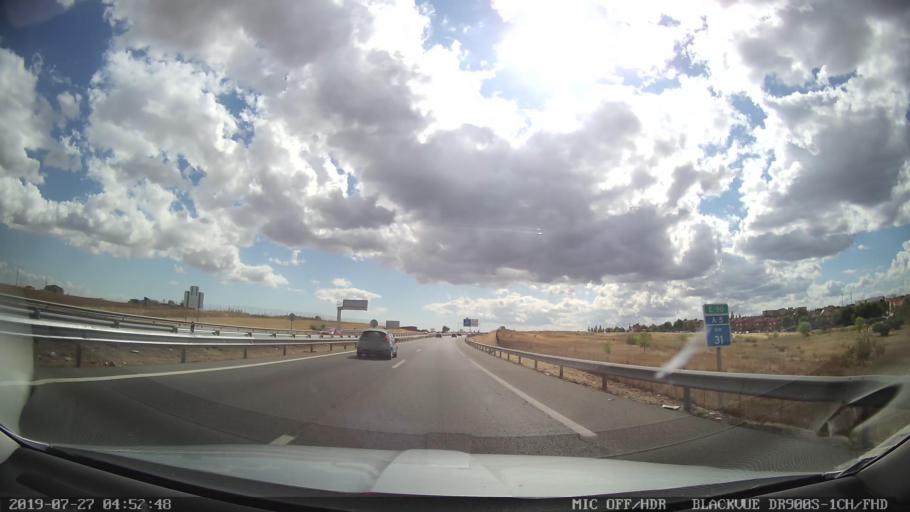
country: ES
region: Madrid
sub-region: Provincia de Madrid
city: Navalcarnero
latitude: 40.2818
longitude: -4.0048
